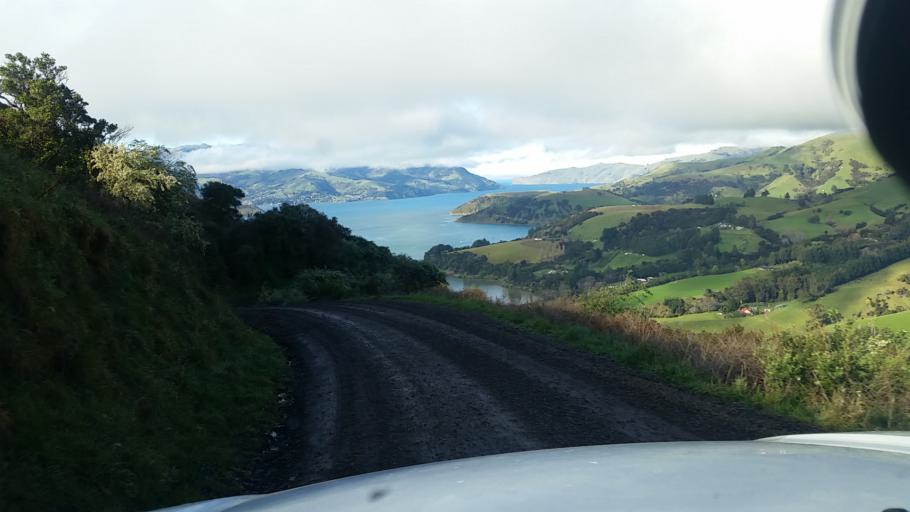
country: NZ
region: Canterbury
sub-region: Christchurch City
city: Christchurch
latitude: -43.7494
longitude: 172.9077
